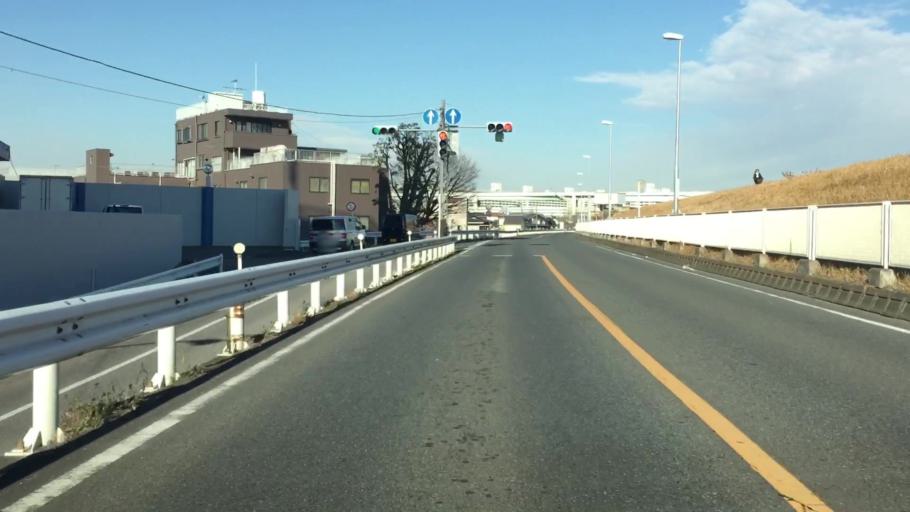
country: JP
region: Saitama
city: Kawaguchi
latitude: 35.7591
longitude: 139.7616
